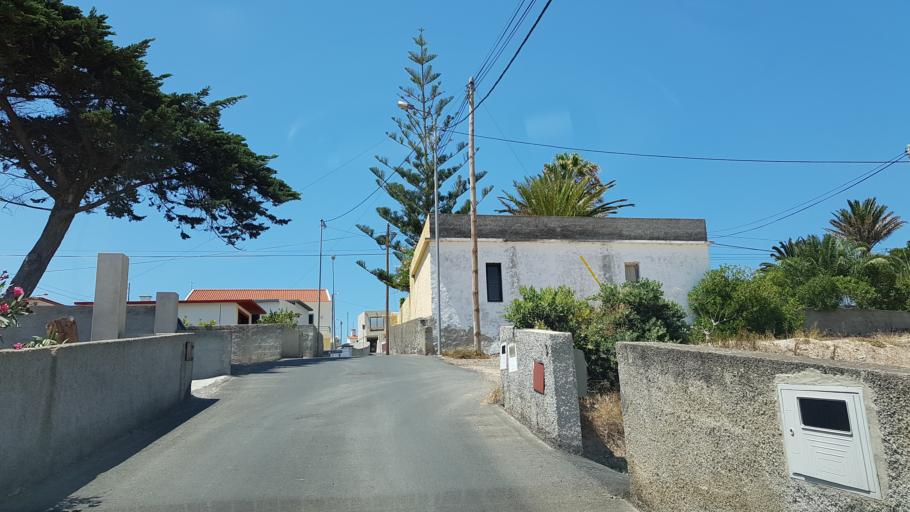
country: PT
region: Madeira
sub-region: Porto Santo
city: Camacha
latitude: 33.0856
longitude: -16.3450
